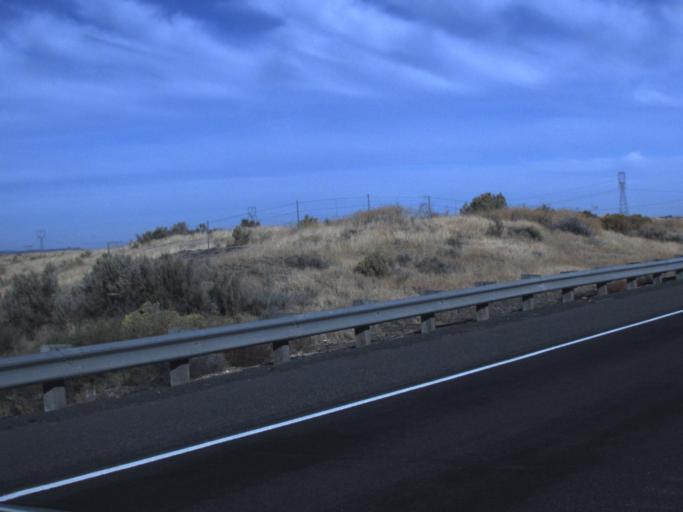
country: US
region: Washington
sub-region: Franklin County
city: Connell
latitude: 46.6357
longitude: -119.0063
